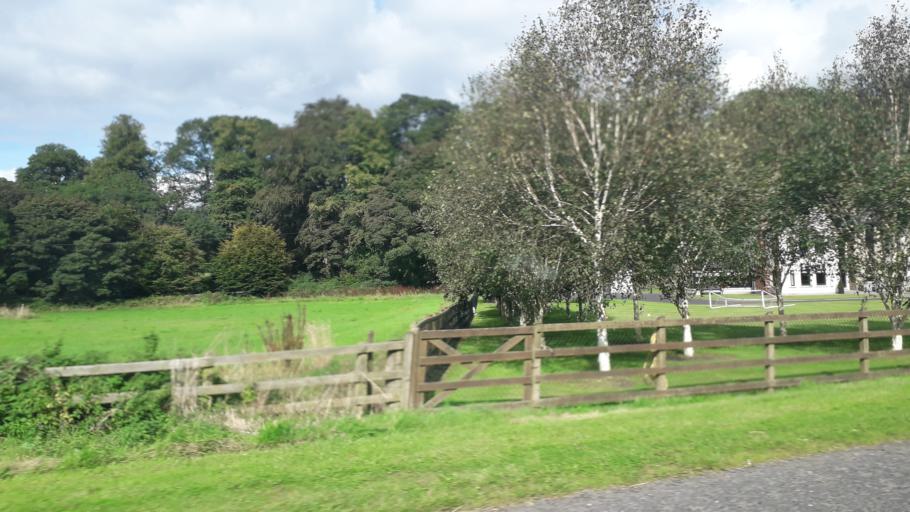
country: IE
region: Leinster
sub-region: Lu
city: Dundalk
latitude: 54.0334
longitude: -6.3634
